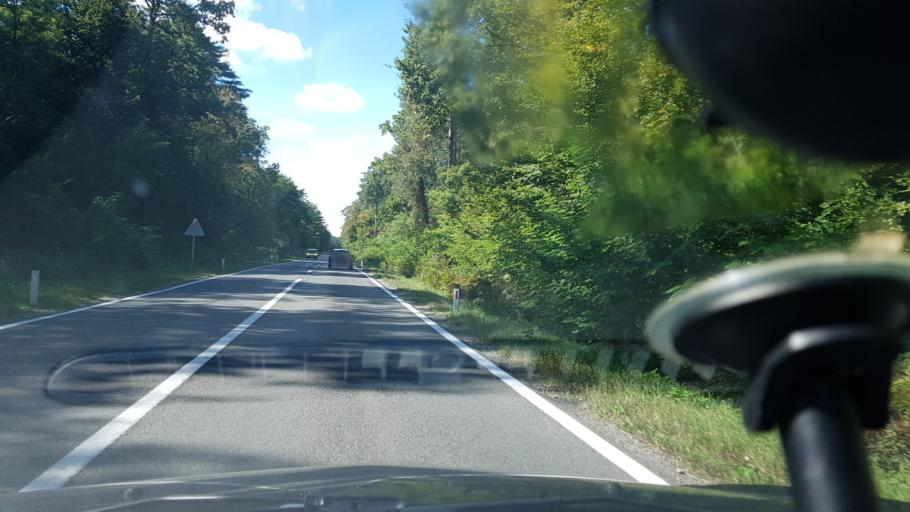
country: SI
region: Kidricevo
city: Kidricevo
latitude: 46.4113
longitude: 15.7900
